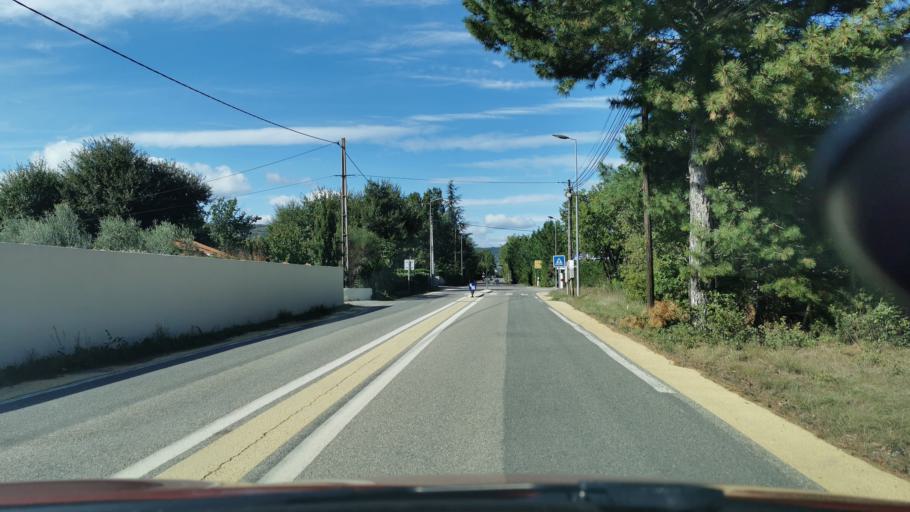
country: FR
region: Provence-Alpes-Cote d'Azur
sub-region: Departement des Alpes-de-Haute-Provence
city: Peipin
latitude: 44.1565
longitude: 5.9714
